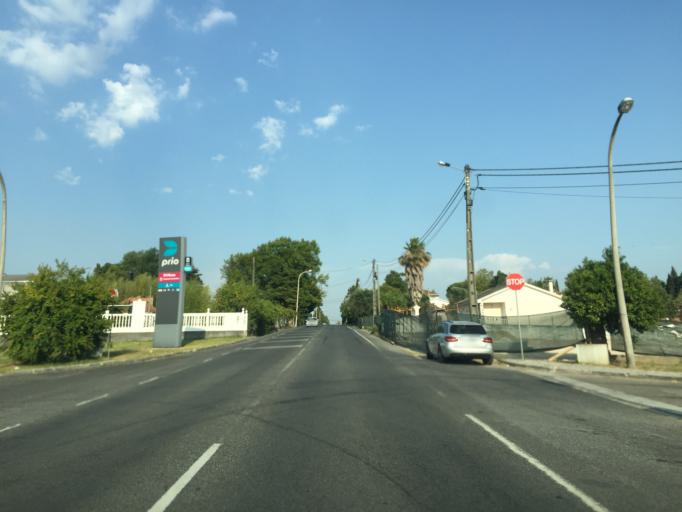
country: PT
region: Santarem
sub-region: Torres Novas
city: Torres Novas
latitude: 39.4765
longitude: -8.5655
